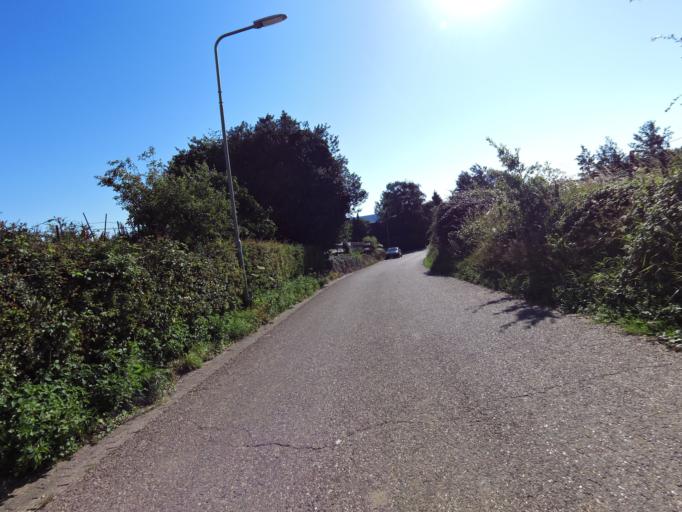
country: NL
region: Limburg
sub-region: Gemeente Vaals
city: Vaals
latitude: 50.7817
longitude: 5.9742
